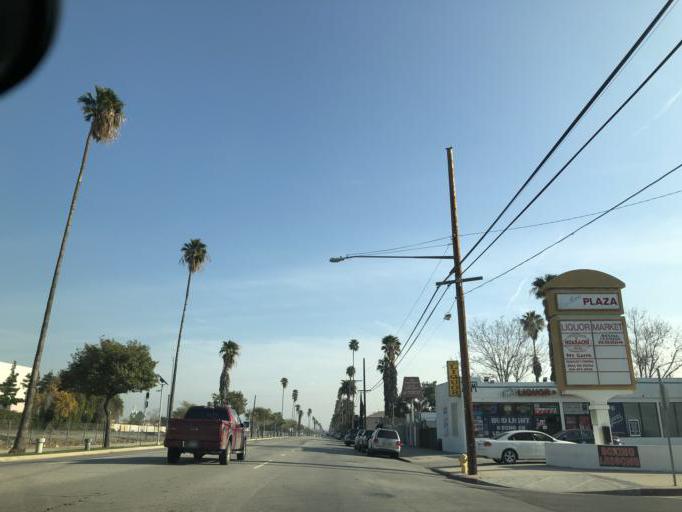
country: US
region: California
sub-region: Los Angeles County
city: San Fernando
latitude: 34.3093
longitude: -118.4725
